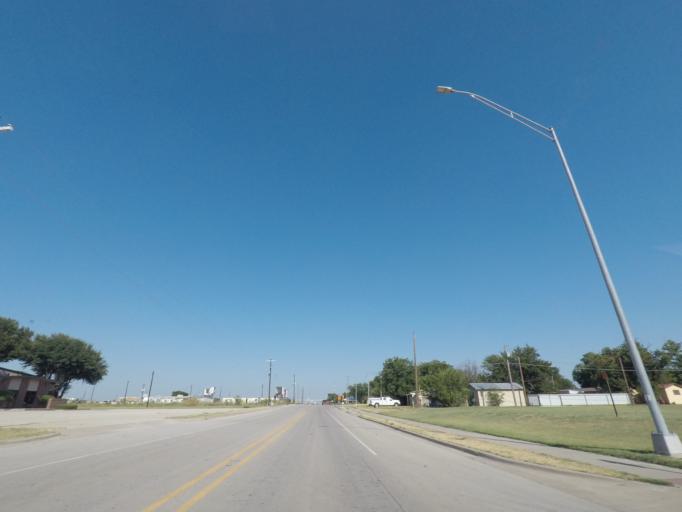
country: US
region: Texas
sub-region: Baylor County
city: Seymour
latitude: 33.5960
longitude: -99.2483
